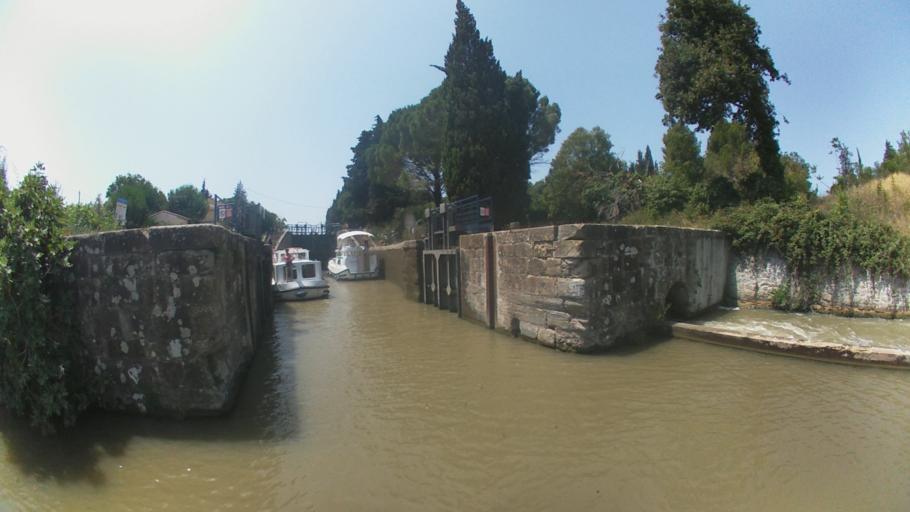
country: FR
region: Languedoc-Roussillon
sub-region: Departement de l'Aude
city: Puicheric
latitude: 43.2311
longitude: 2.6390
